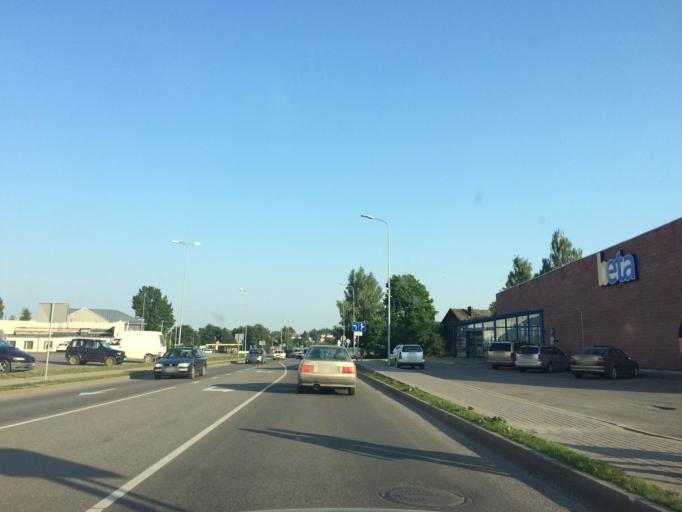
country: LV
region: Rezekne
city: Rezekne
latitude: 56.5174
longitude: 27.3497
